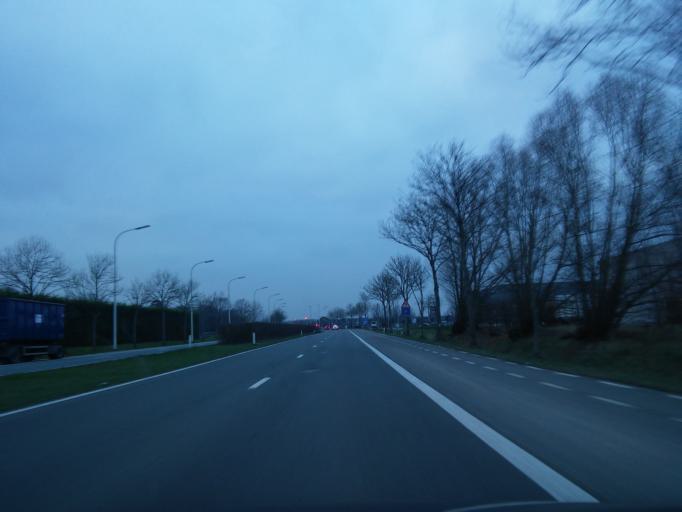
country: BE
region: Flanders
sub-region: Provincie Oost-Vlaanderen
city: Zele
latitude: 51.0814
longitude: 4.0401
